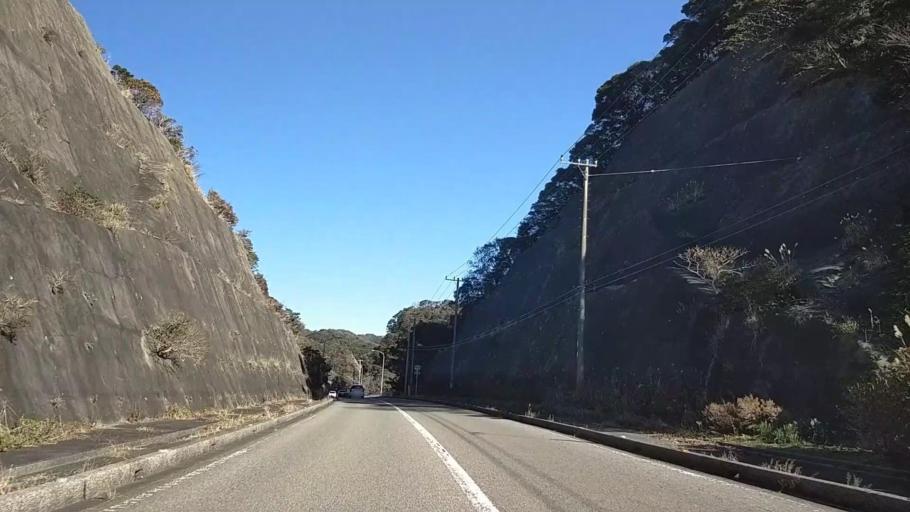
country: JP
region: Chiba
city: Katsuura
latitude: 35.1408
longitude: 140.2575
